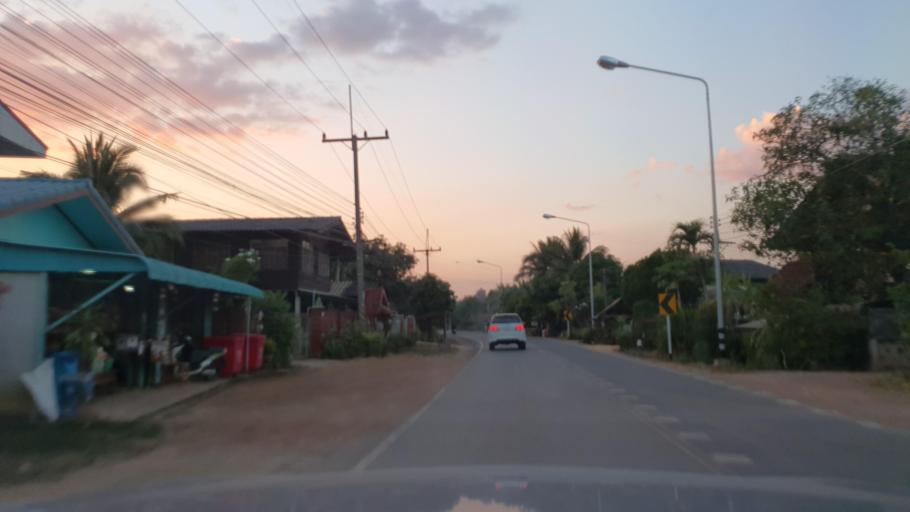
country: TH
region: Phayao
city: Dok Kham Tai
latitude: 19.0433
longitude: 100.0614
